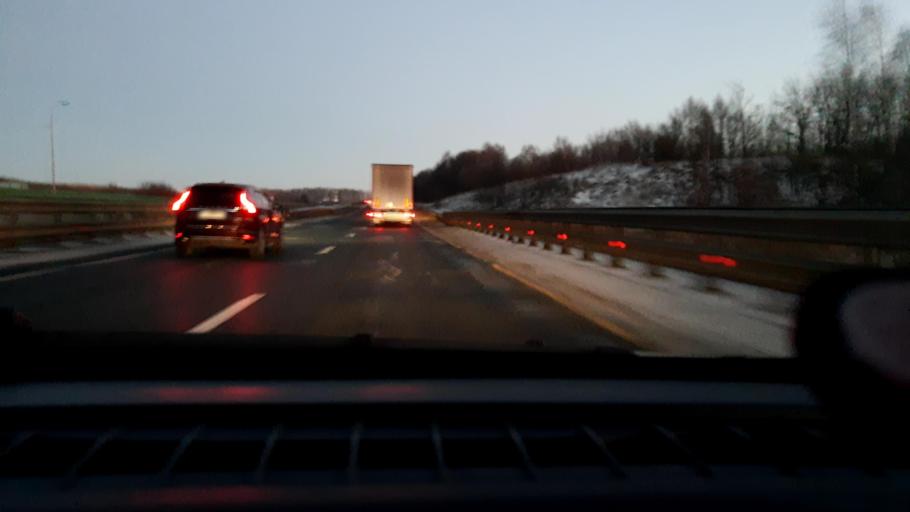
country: RU
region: Nizjnij Novgorod
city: Lyskovo
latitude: 56.0105
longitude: 44.9290
